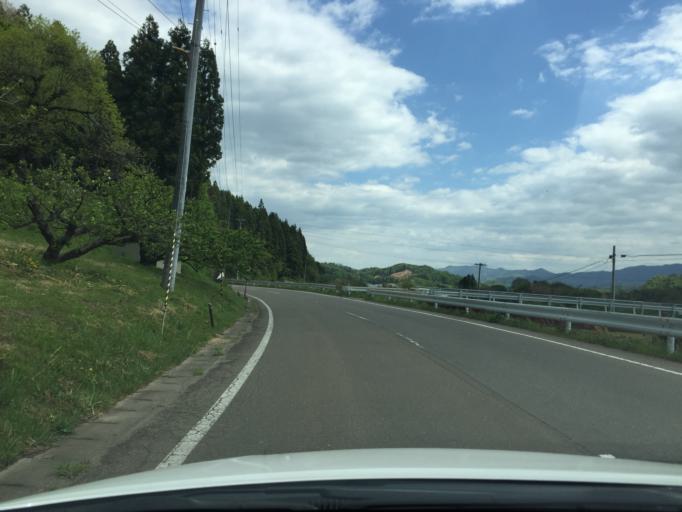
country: JP
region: Fukushima
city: Hobaramachi
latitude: 37.7595
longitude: 140.5711
